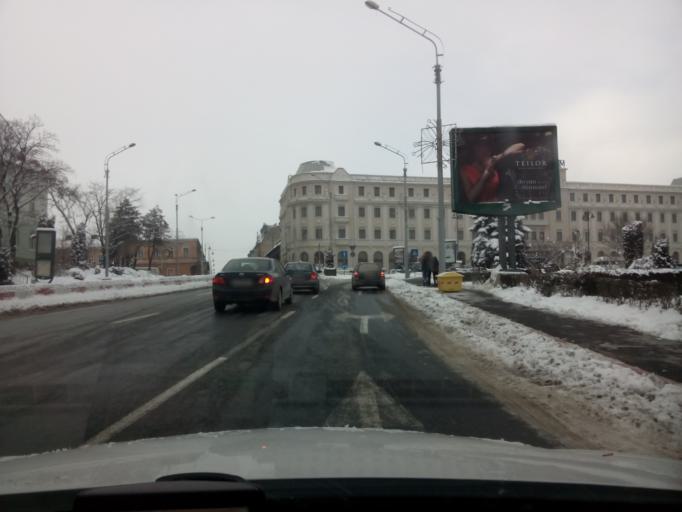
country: RO
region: Sibiu
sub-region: Municipiul Sibiu
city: Sibiu
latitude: 45.7912
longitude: 24.1484
